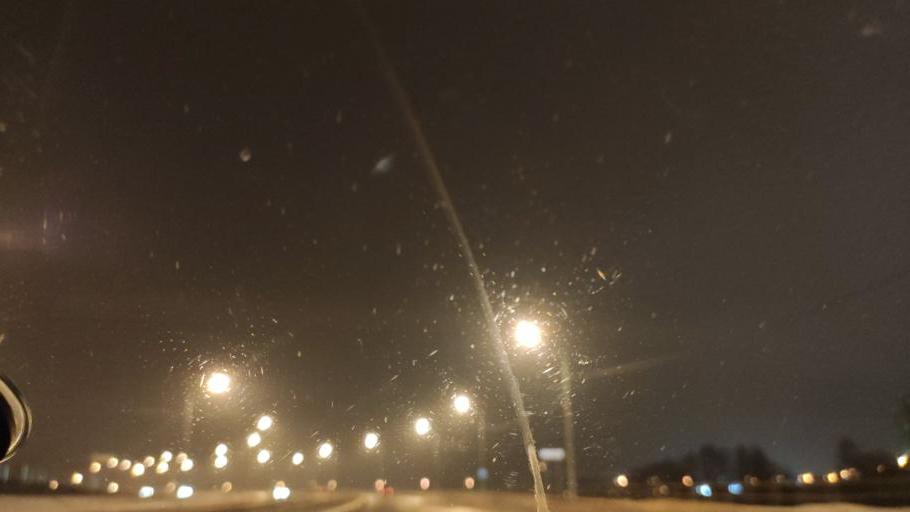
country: RU
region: Moscow
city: Annino
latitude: 55.5253
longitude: 37.6182
